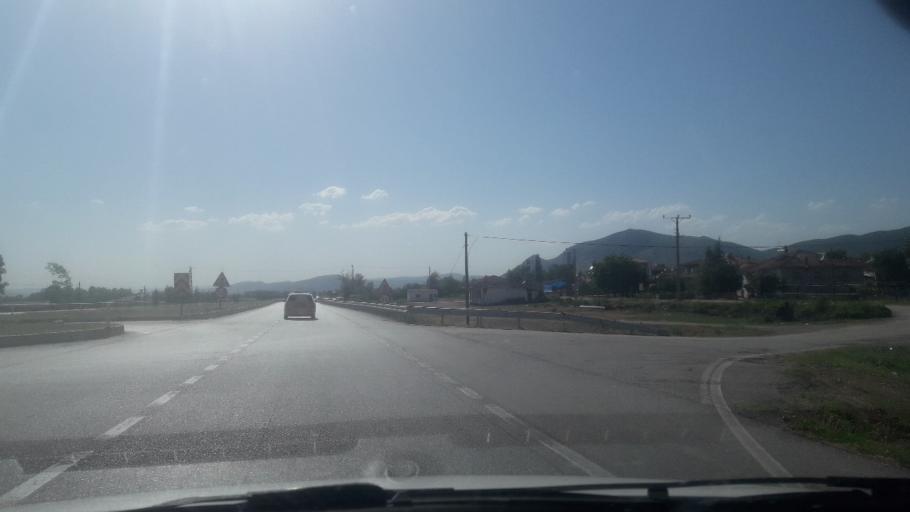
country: TR
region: Tokat
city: Dokmetepe
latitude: 40.3134
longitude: 36.2640
